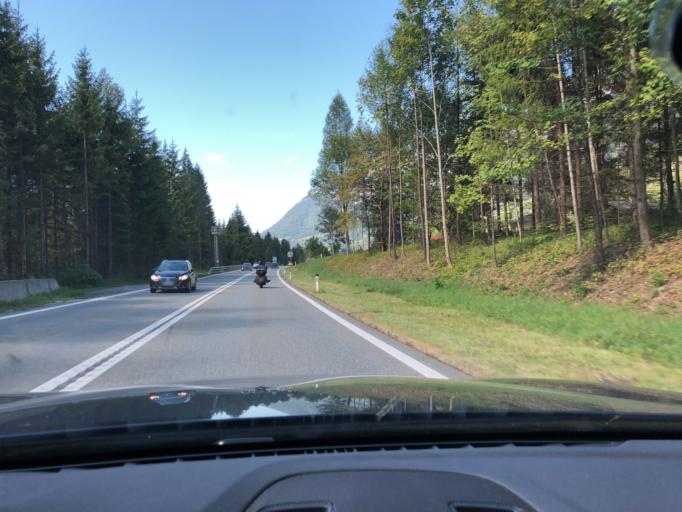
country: AT
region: Vorarlberg
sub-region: Politischer Bezirk Bludenz
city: Innerbraz
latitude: 47.1377
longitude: 9.9334
